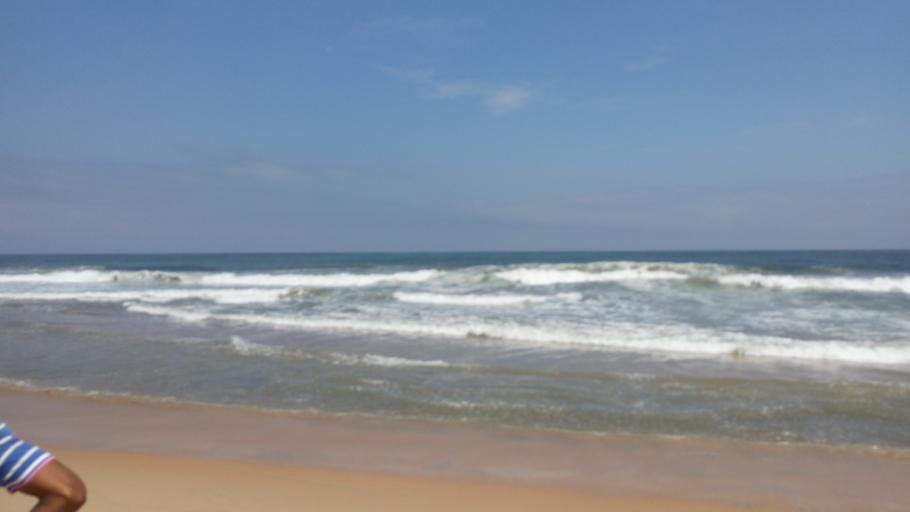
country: CI
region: Sud-Comoe
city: Grand-Bassam
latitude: 5.1874
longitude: -3.6946
